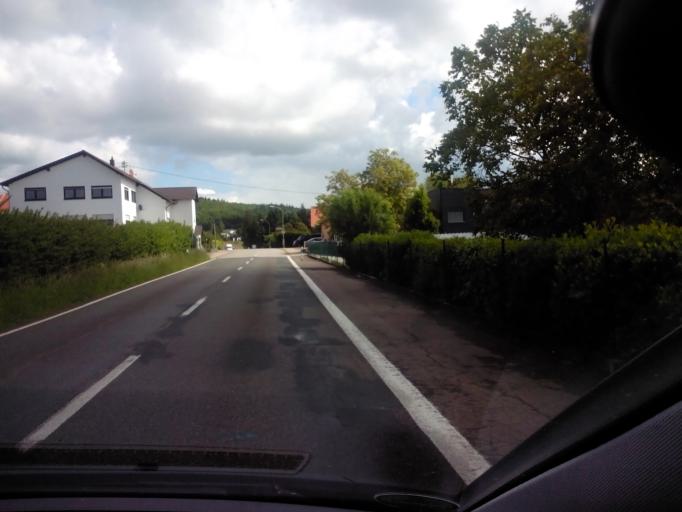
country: DE
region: Saarland
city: Schmelz
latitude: 49.3831
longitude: 6.8585
